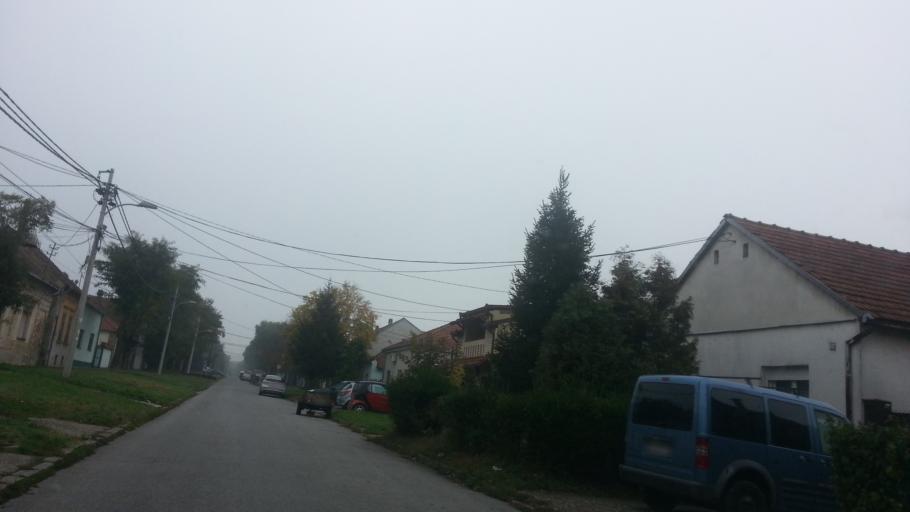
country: RS
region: Central Serbia
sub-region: Belgrade
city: Zemun
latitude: 44.8536
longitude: 20.3952
